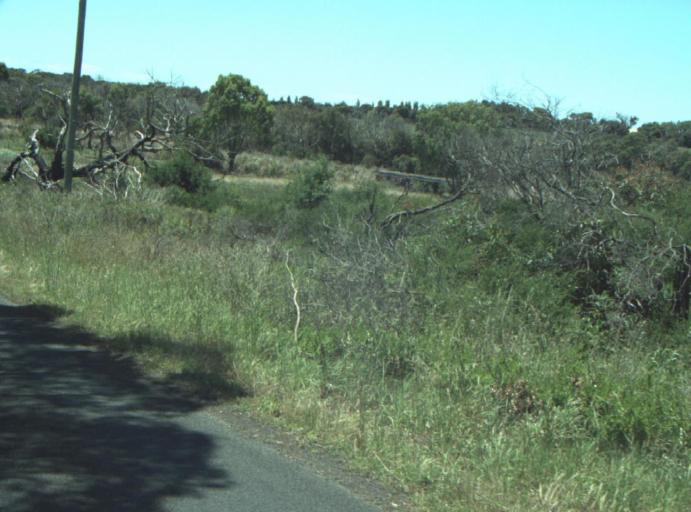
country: AU
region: Victoria
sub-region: Greater Geelong
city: Clifton Springs
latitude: -38.2330
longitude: 144.5801
